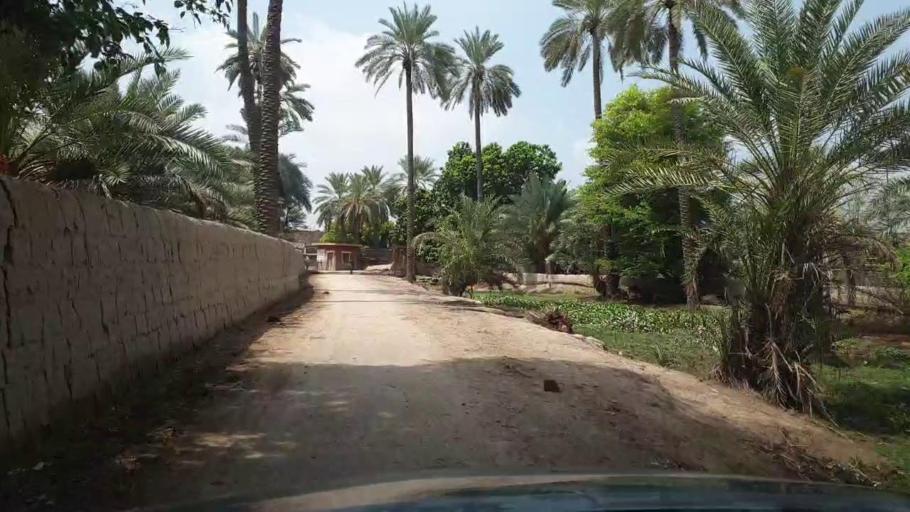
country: PK
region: Sindh
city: Pir jo Goth
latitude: 27.6131
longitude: 68.6748
